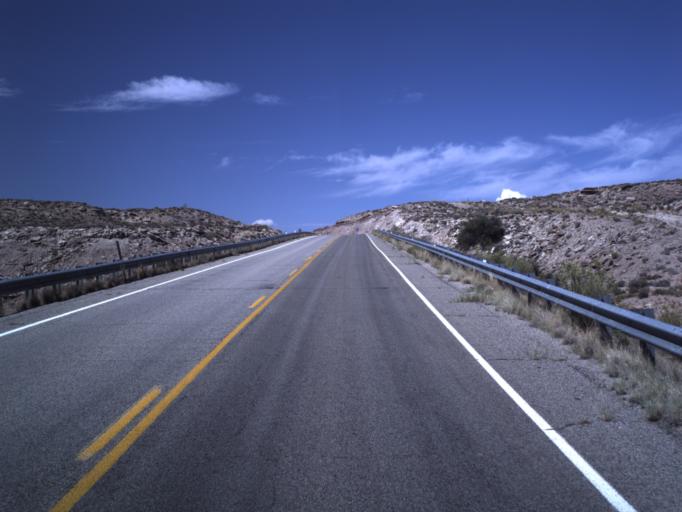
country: US
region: Utah
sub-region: San Juan County
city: Blanding
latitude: 37.2735
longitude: -109.3459
